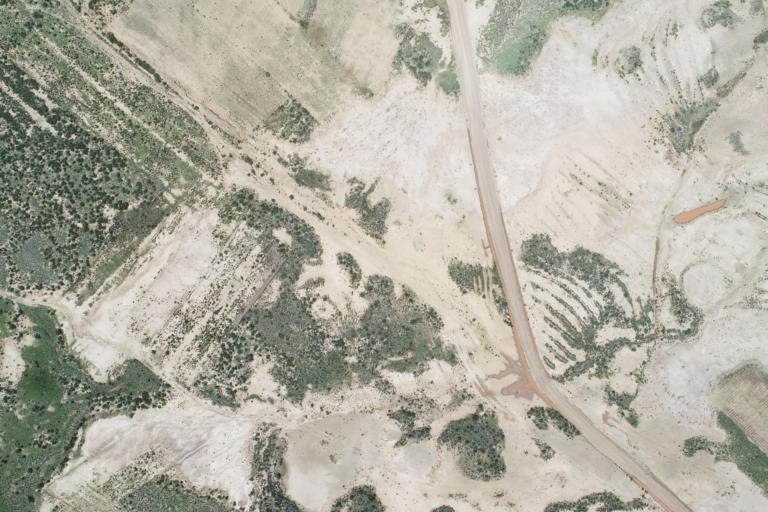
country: BO
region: La Paz
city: Curahuara de Carangas
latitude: -17.3169
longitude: -68.4989
